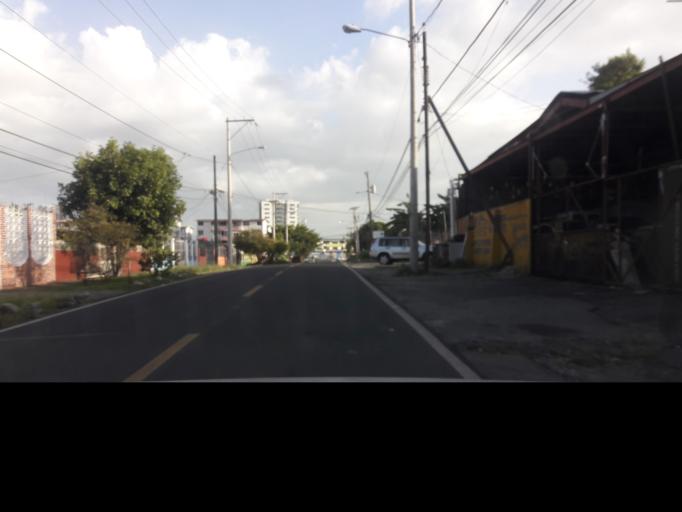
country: PA
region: Panama
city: San Miguelito
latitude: 9.0220
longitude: -79.4931
